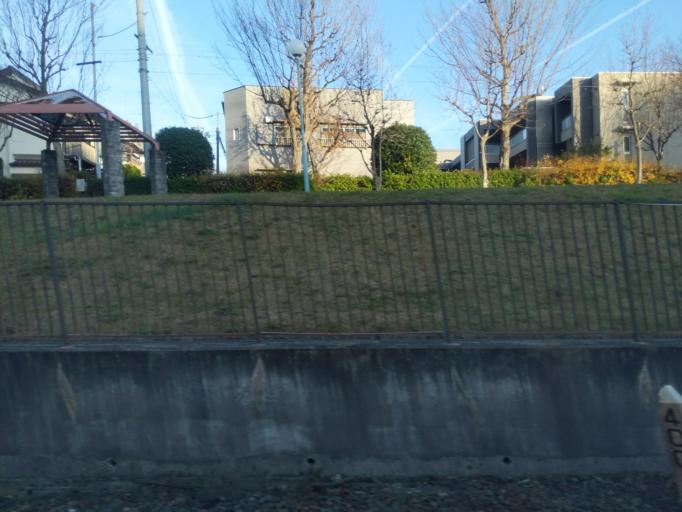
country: JP
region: Aichi
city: Nagoya-shi
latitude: 35.1837
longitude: 136.9372
